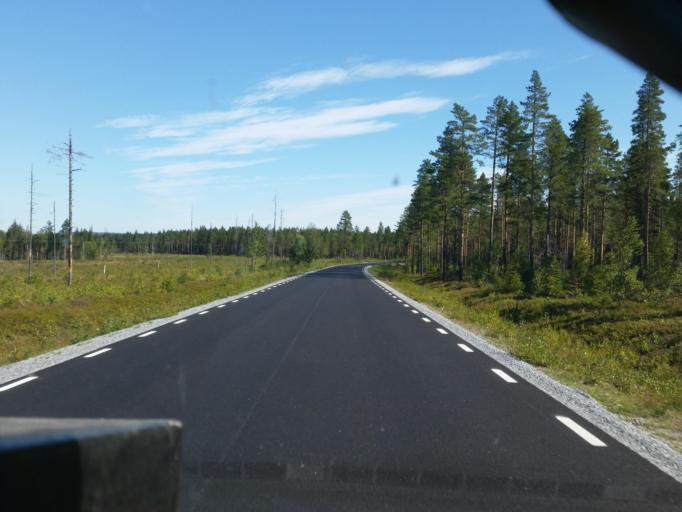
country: SE
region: Norrbotten
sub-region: Pitea Kommun
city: Roknas
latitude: 65.3486
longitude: 21.0145
